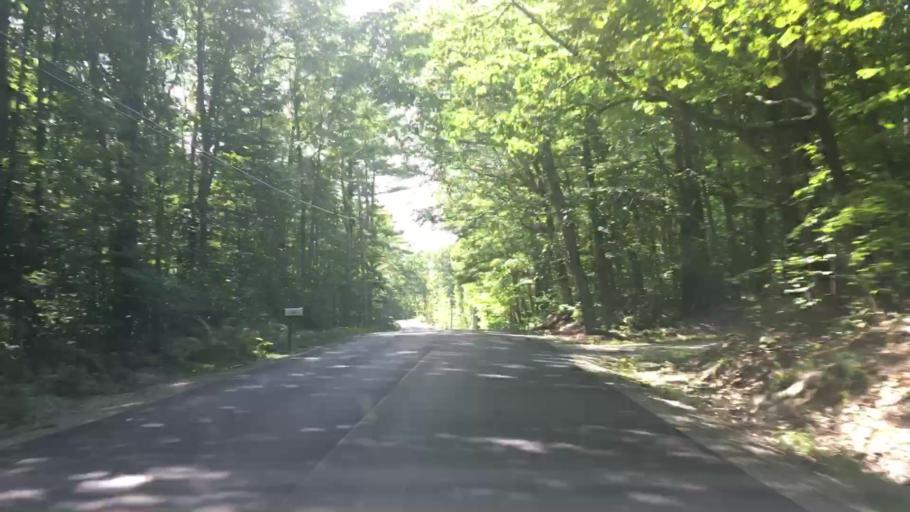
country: US
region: Maine
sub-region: Androscoggin County
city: Poland
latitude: 44.0126
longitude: -70.3975
